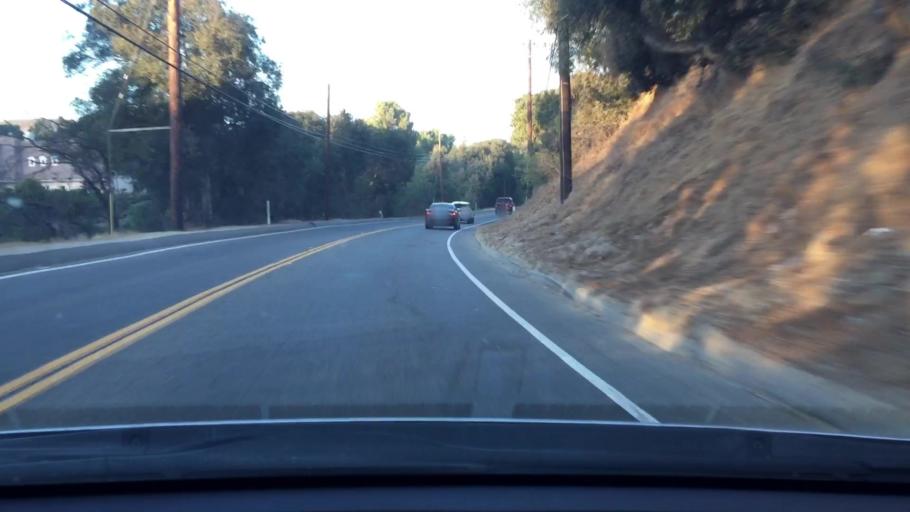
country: US
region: California
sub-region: San Bernardino County
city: Chino Hills
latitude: 33.9556
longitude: -117.7727
